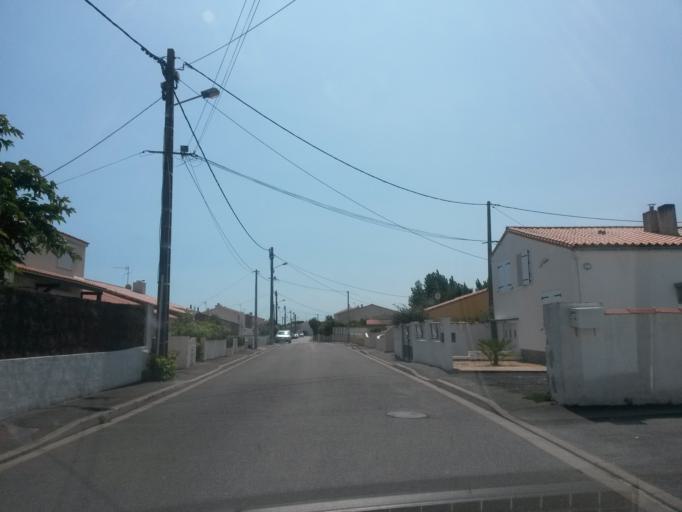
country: FR
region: Pays de la Loire
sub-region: Departement de la Vendee
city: Les Sables-d'Olonne
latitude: 46.5100
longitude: -1.8074
